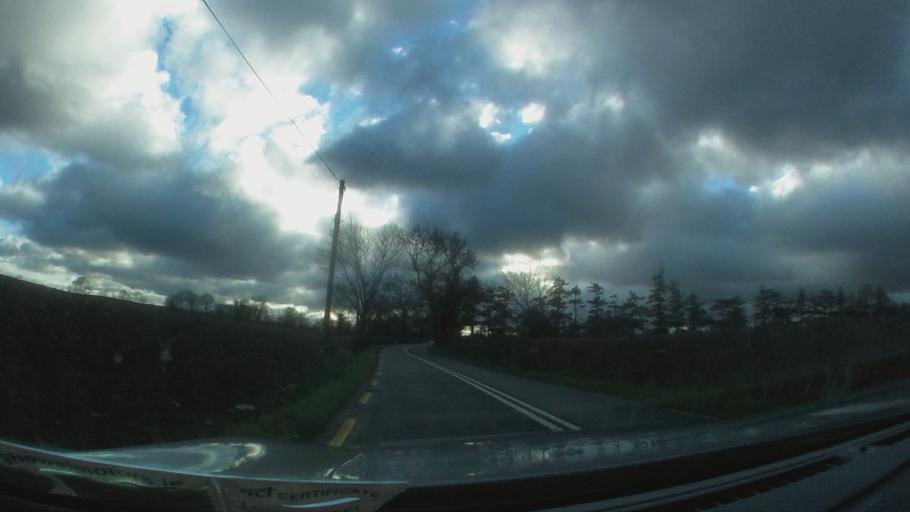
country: IE
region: Leinster
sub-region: Kilkenny
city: Thomastown
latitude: 52.5691
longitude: -7.1162
